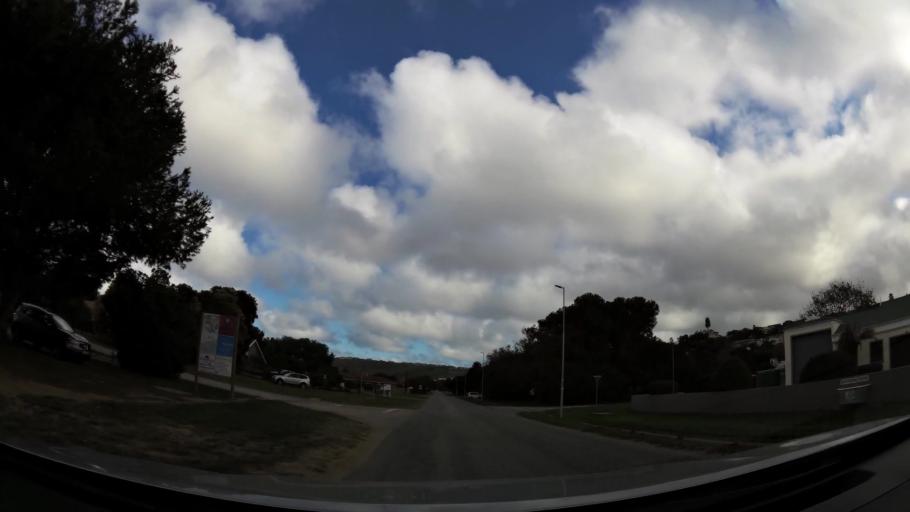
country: ZA
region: Western Cape
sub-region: Eden District Municipality
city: Plettenberg Bay
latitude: -34.0745
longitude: 23.3664
